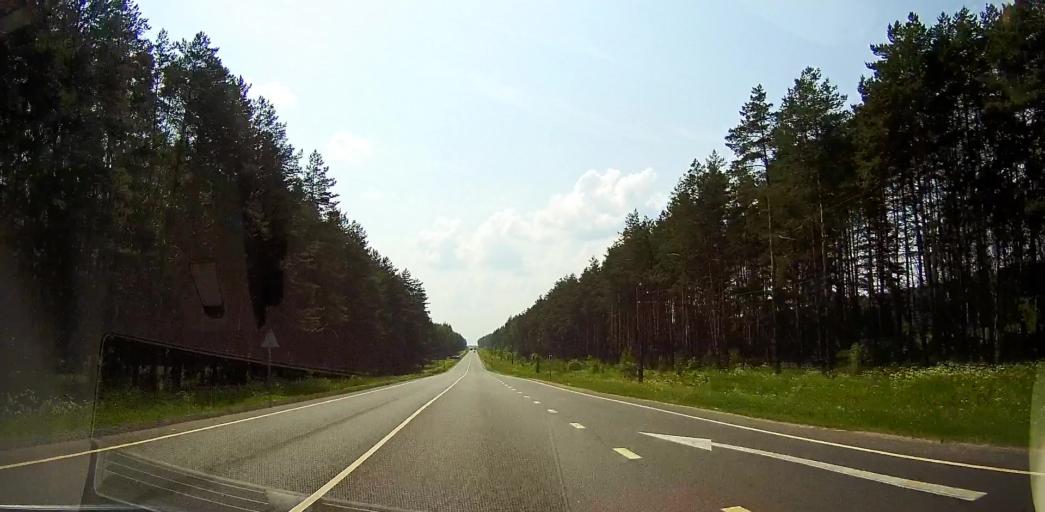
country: RU
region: Moskovskaya
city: Meshcherino
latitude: 55.1717
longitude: 38.3297
